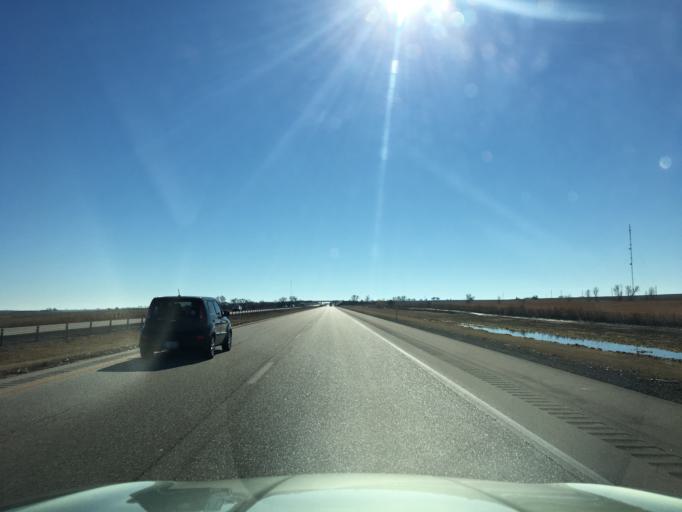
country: US
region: Oklahoma
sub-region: Kay County
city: Blackwell
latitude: 36.8902
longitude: -97.3533
